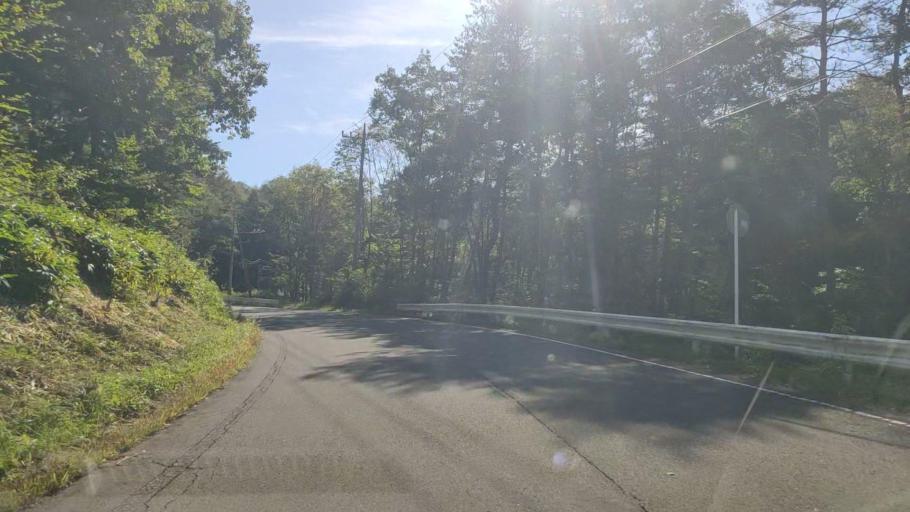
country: JP
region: Gunma
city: Nakanojomachi
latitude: 36.6063
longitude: 138.6783
